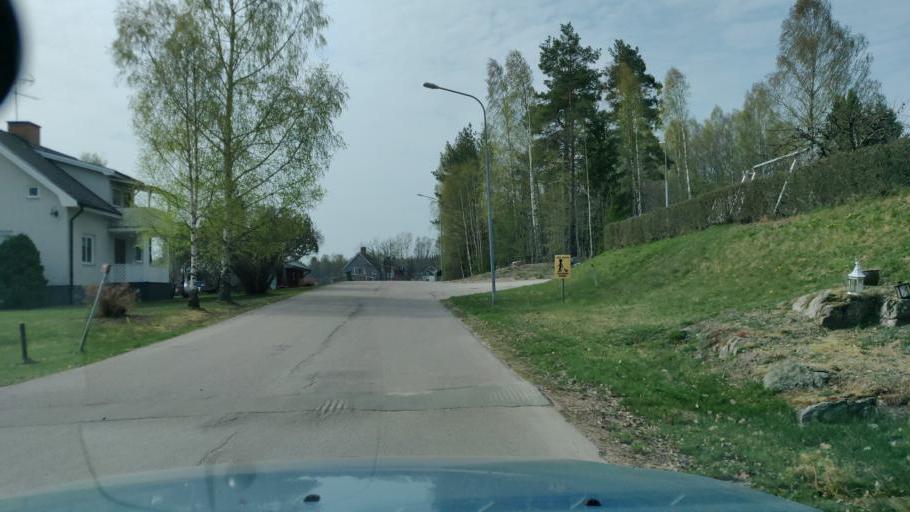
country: SE
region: Vaermland
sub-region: Munkfors Kommun
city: Munkfors
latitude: 59.8346
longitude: 13.5166
